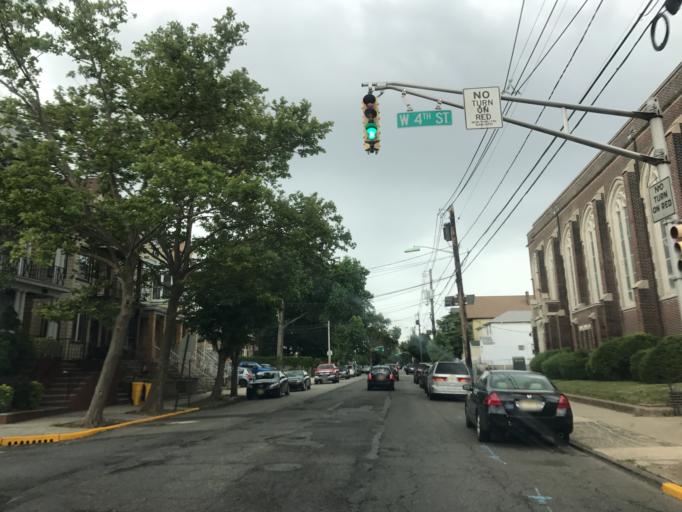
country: US
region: New Jersey
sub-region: Hudson County
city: Bayonne
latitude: 40.6501
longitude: -74.1283
